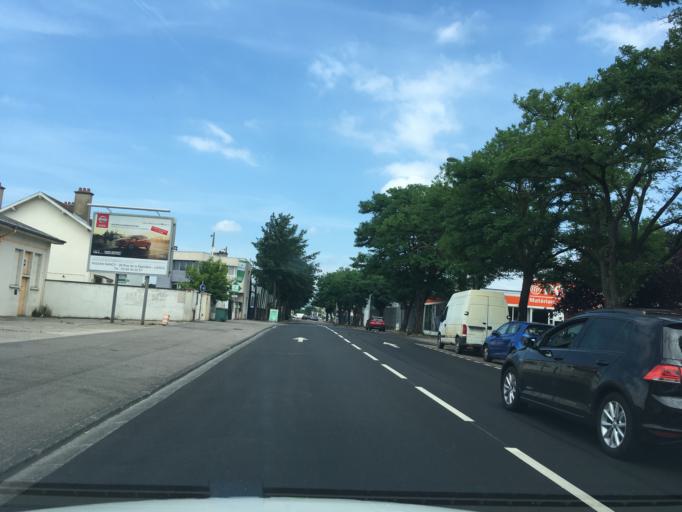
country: FR
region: Lorraine
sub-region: Departement de Meurthe-et-Moselle
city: Tomblaine
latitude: 48.6880
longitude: 6.2052
